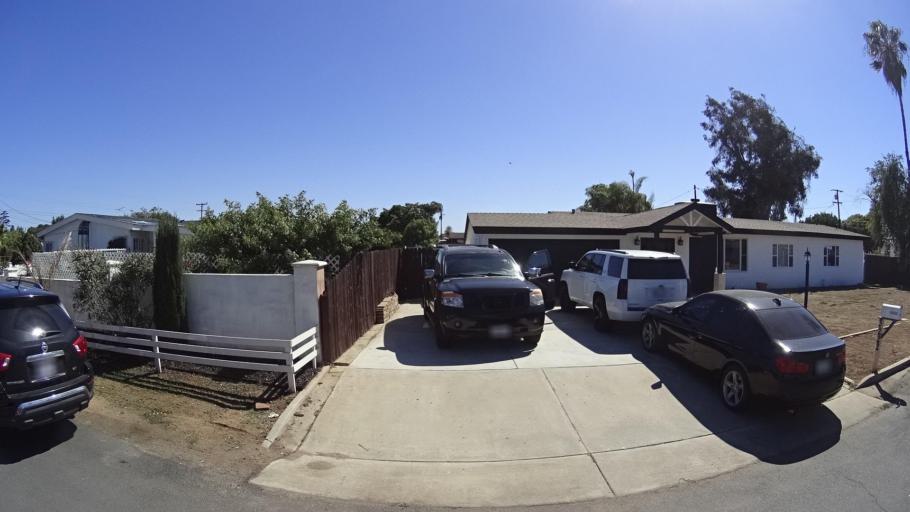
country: US
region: California
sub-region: San Diego County
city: Bonita
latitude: 32.6544
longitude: -117.0571
